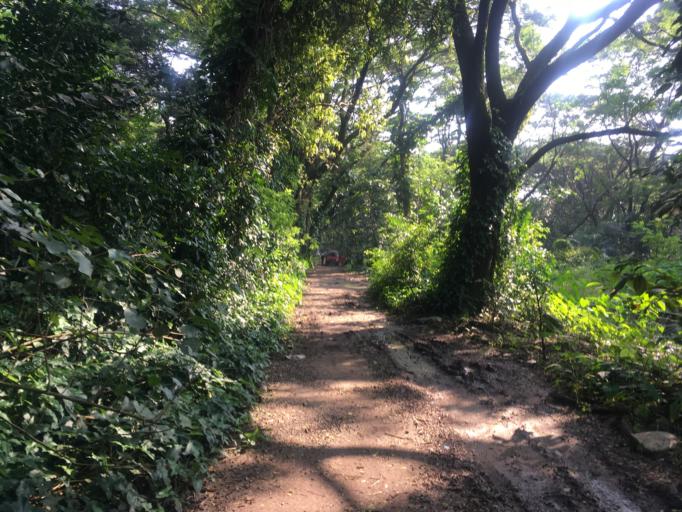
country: IN
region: Kerala
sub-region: Ernakulam
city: Cochin
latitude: 9.9916
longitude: 76.2765
